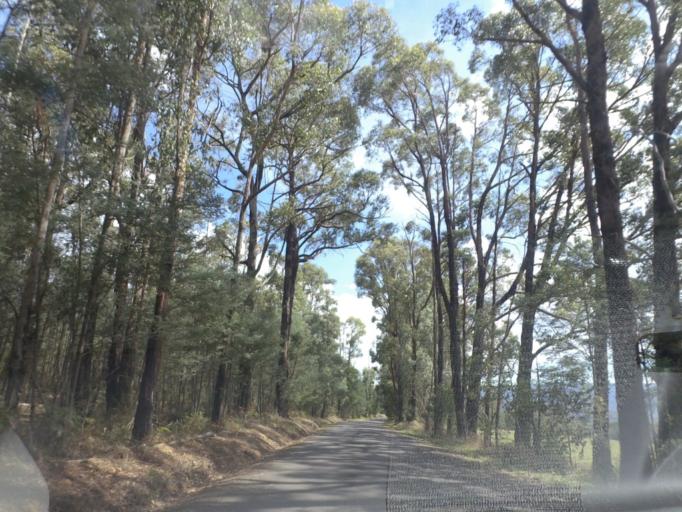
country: AU
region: Victoria
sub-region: Murrindindi
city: Alexandra
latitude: -37.4486
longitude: 145.7460
